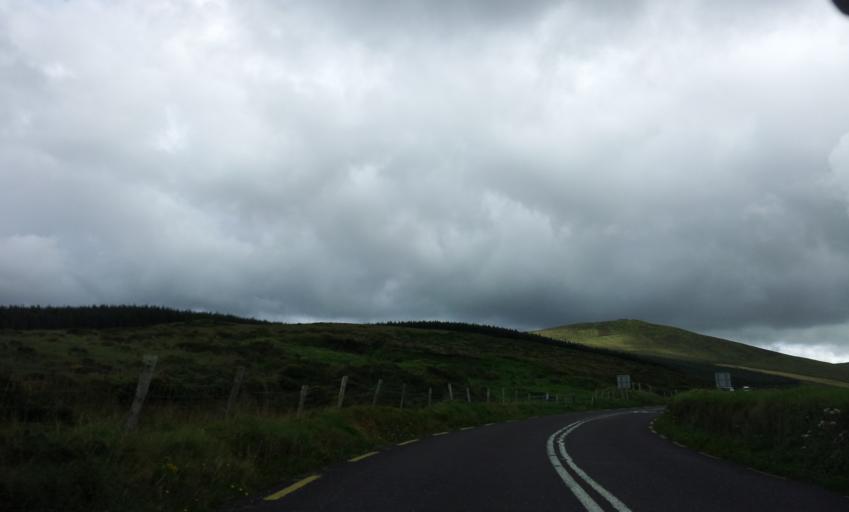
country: IE
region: Munster
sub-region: Ciarrai
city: Killorglin
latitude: 52.2136
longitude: -9.9389
